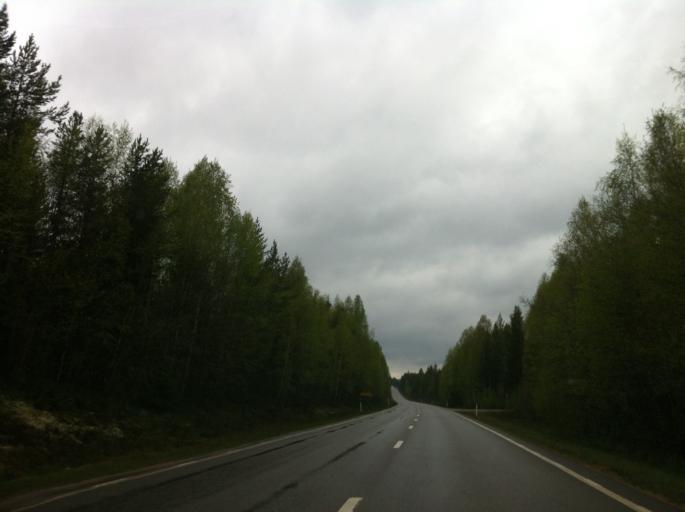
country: SE
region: Jaemtland
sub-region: Harjedalens Kommun
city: Sveg
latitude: 62.0973
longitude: 14.2296
